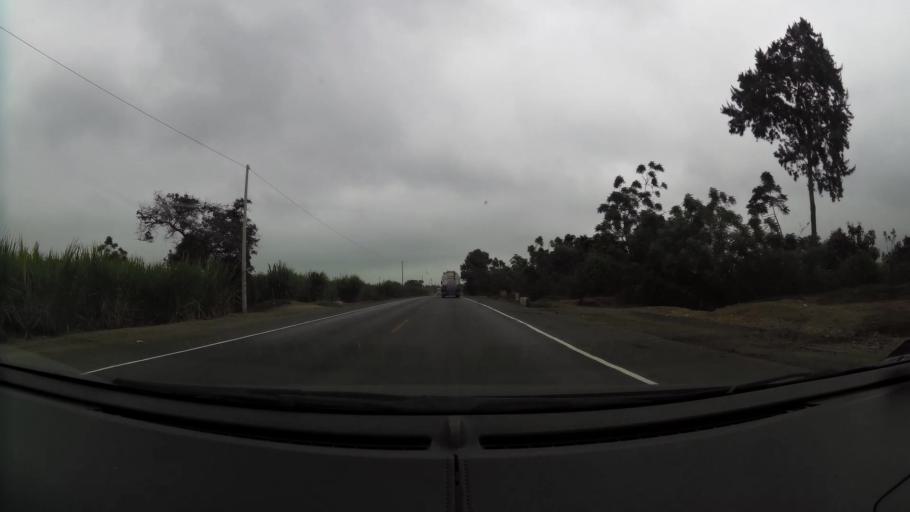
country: PE
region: La Libertad
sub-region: Viru
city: Viru
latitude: -8.4381
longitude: -78.7596
